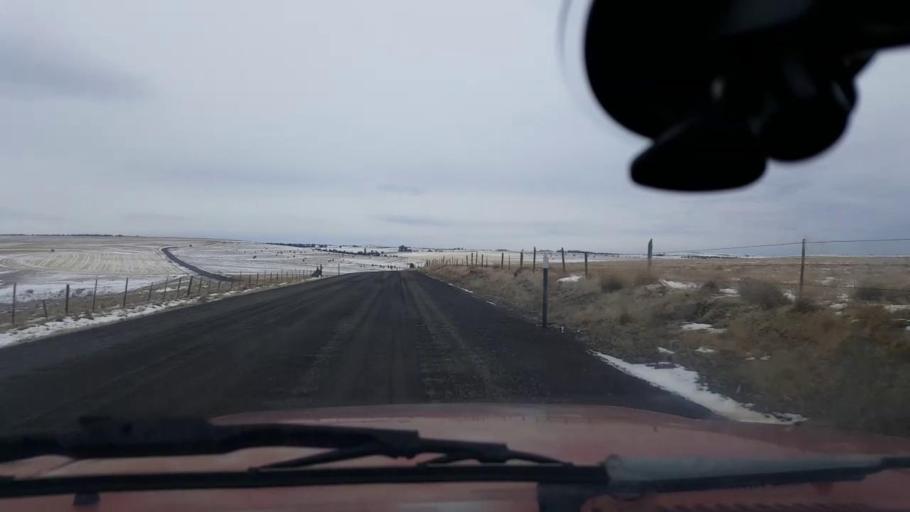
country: US
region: Washington
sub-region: Garfield County
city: Pomeroy
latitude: 46.3202
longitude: -117.4130
